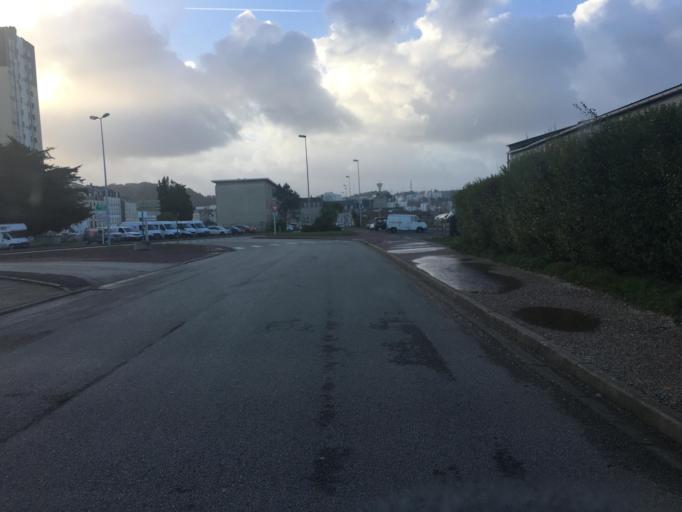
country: FR
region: Lower Normandy
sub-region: Departement de la Manche
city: Cherbourg-Octeville
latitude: 49.6424
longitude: -1.6179
